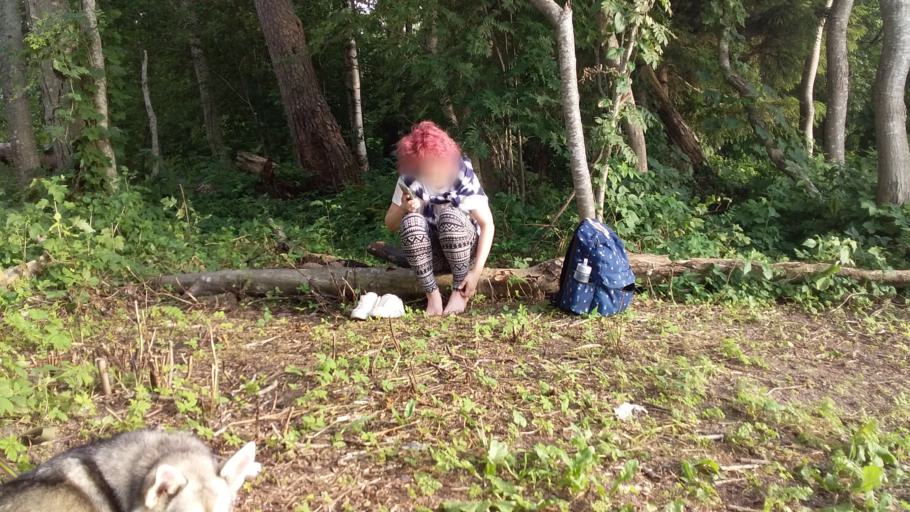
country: RU
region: Novgorod
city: Valday
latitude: 57.9865
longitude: 33.2981
